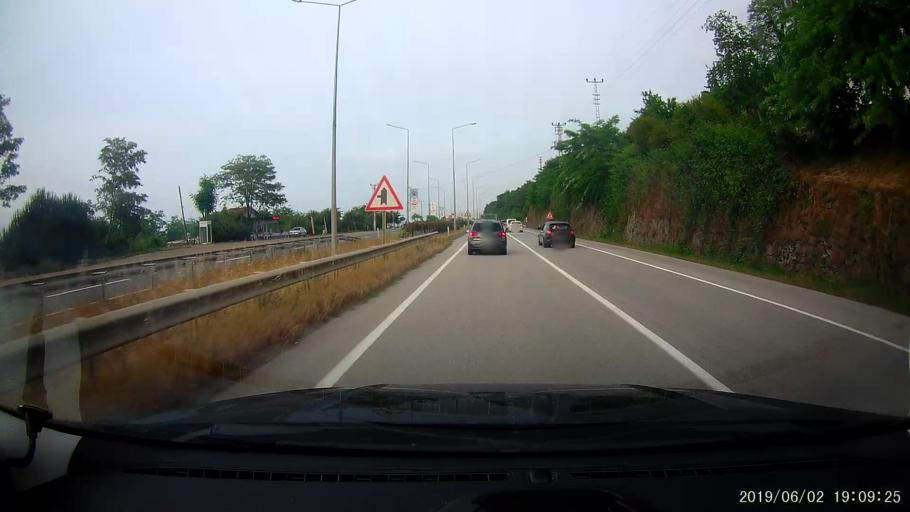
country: TR
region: Ordu
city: Gulyali
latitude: 40.9729
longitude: 38.0280
